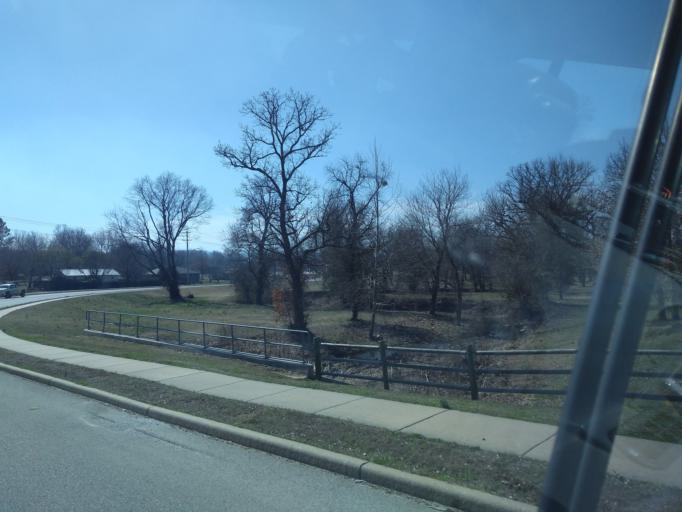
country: US
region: Arkansas
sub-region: Washington County
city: Farmington
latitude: 36.0463
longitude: -94.2358
